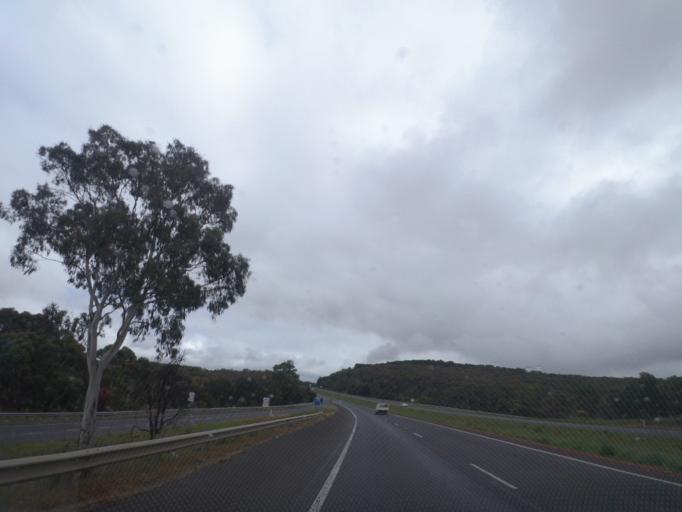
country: AU
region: Victoria
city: Brown Hill
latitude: -37.5494
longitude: 143.9061
